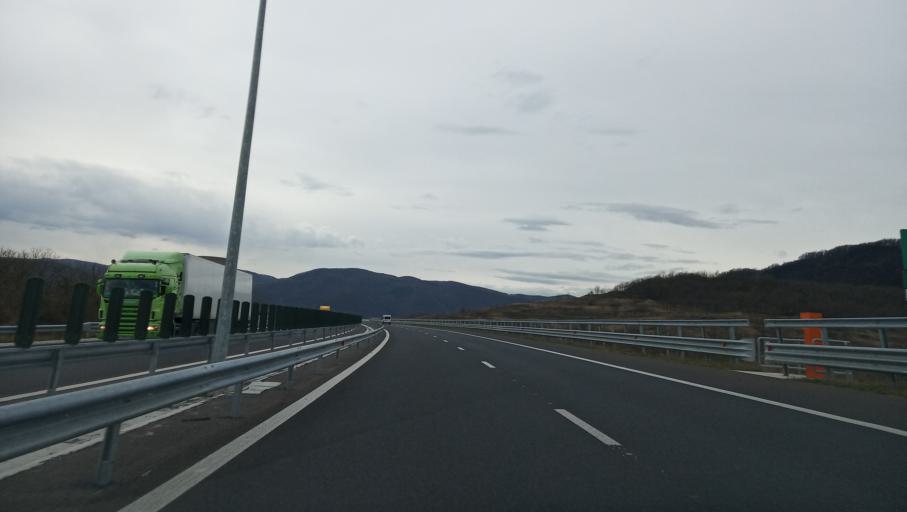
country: RO
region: Hunedoara
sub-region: Comuna Vetel
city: Vetel
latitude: 45.9247
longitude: 22.8299
